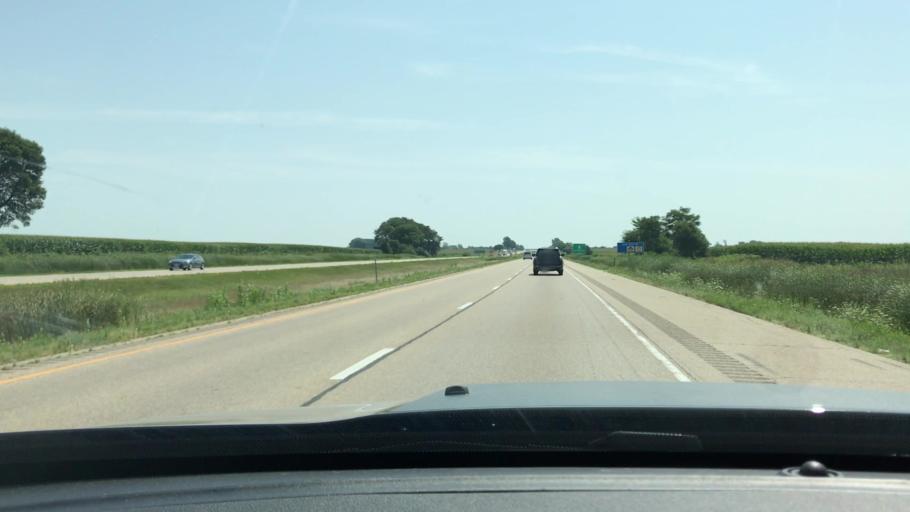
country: US
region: Illinois
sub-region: Bureau County
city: Ladd
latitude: 41.3718
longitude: -89.2431
